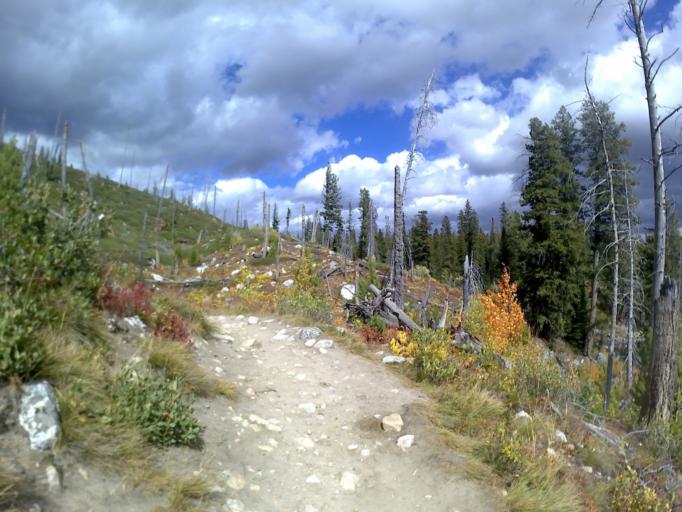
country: US
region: Wyoming
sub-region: Teton County
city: Moose Wilson Road
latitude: 43.7778
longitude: -110.7320
